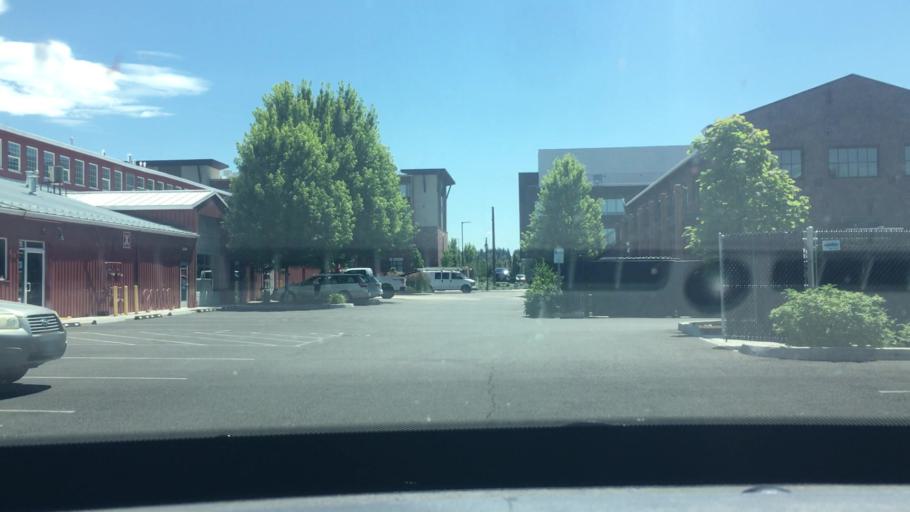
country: US
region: Oregon
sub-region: Deschutes County
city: Bend
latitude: 44.0511
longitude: -121.3160
